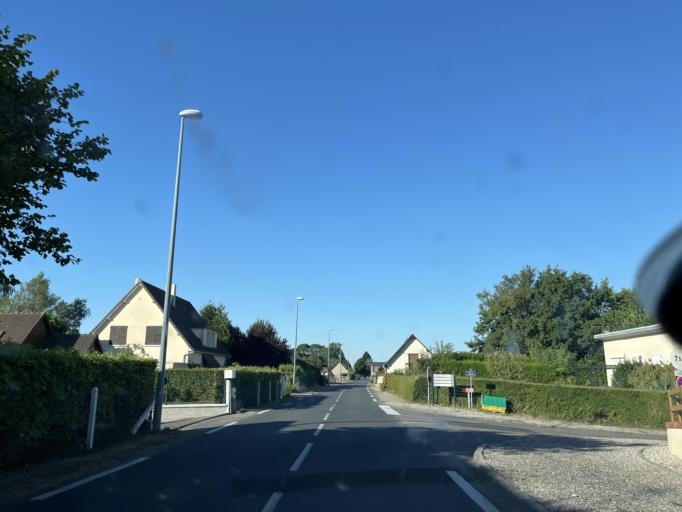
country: FR
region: Haute-Normandie
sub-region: Departement de la Seine-Maritime
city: Lillebonne
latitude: 49.5452
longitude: 0.5596
